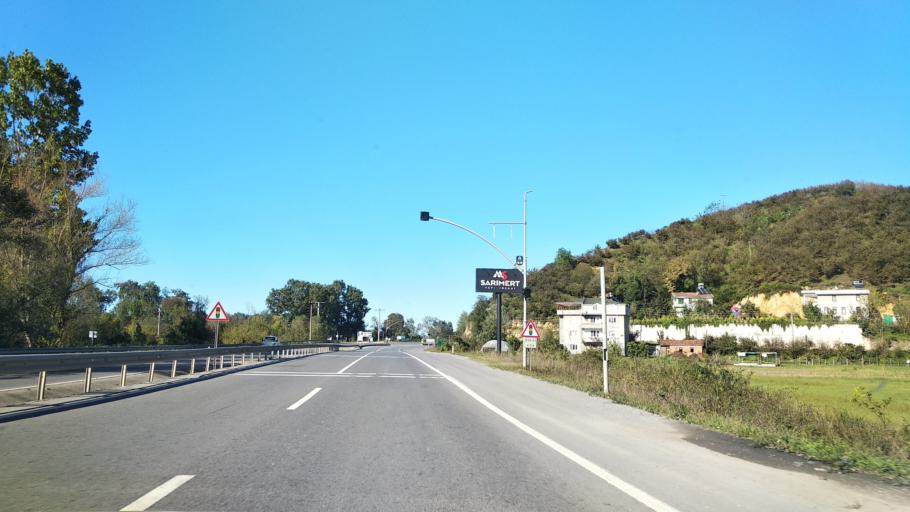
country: TR
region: Sakarya
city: Karasu
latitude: 41.0789
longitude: 30.6460
